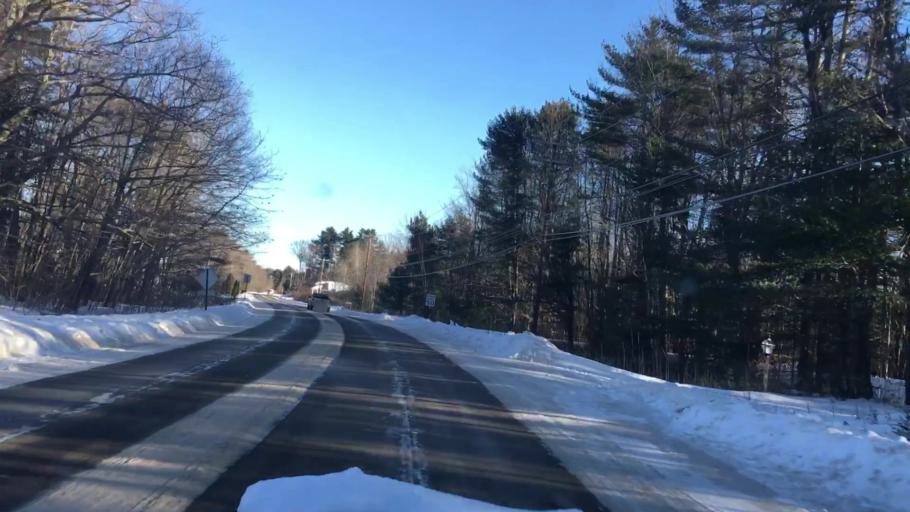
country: US
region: Maine
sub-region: Cumberland County
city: Brunswick
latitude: 43.9424
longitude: -69.9299
